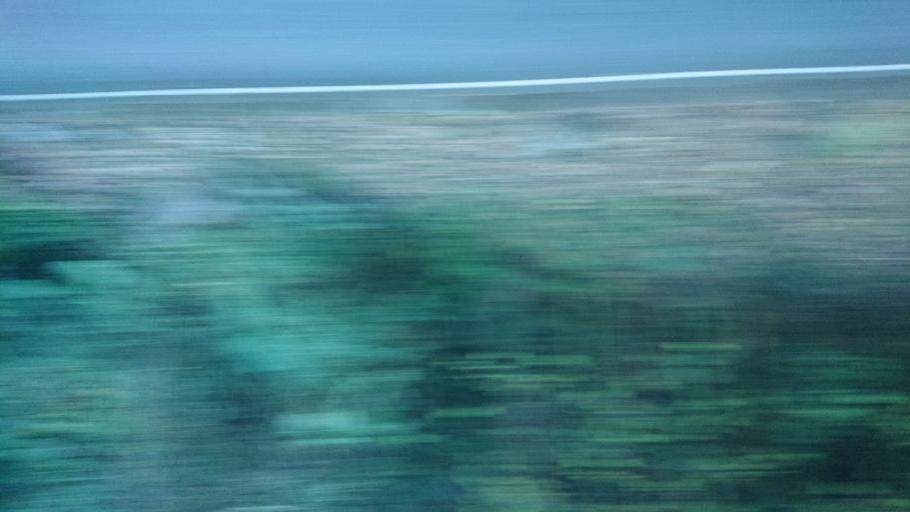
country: TW
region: Taiwan
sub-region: Chiayi
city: Jiayi Shi
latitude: 23.4655
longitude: 120.7183
